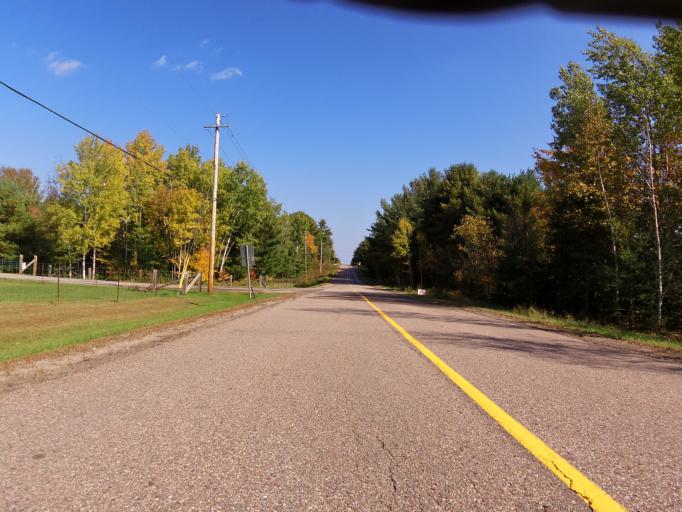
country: CA
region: Ontario
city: Petawawa
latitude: 45.8158
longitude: -77.2493
